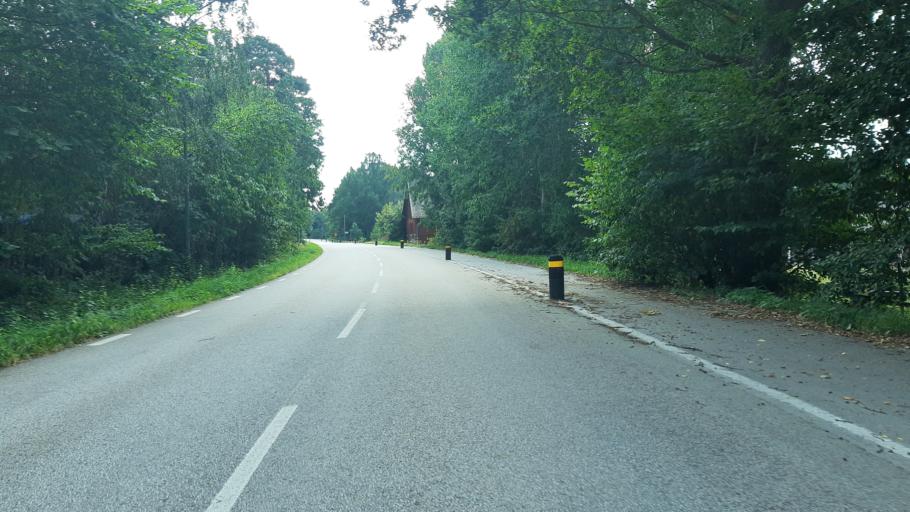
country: SE
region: Blekinge
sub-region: Karlskrona Kommun
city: Nattraby
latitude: 56.2234
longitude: 15.4135
